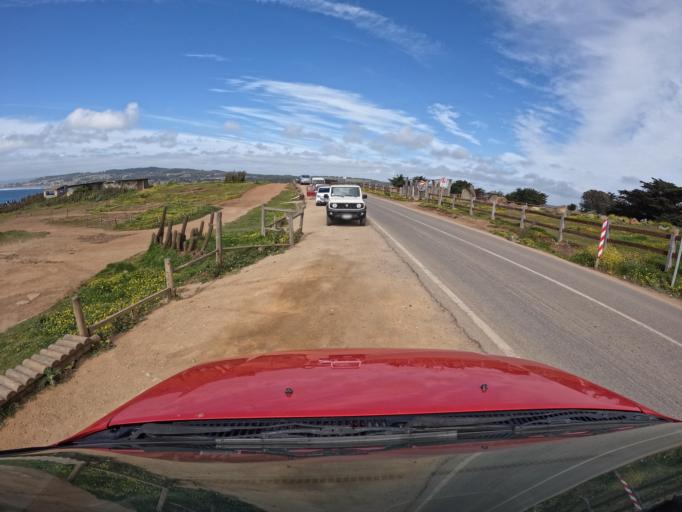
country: CL
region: O'Higgins
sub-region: Provincia de Colchagua
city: Santa Cruz
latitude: -34.4257
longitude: -72.0462
